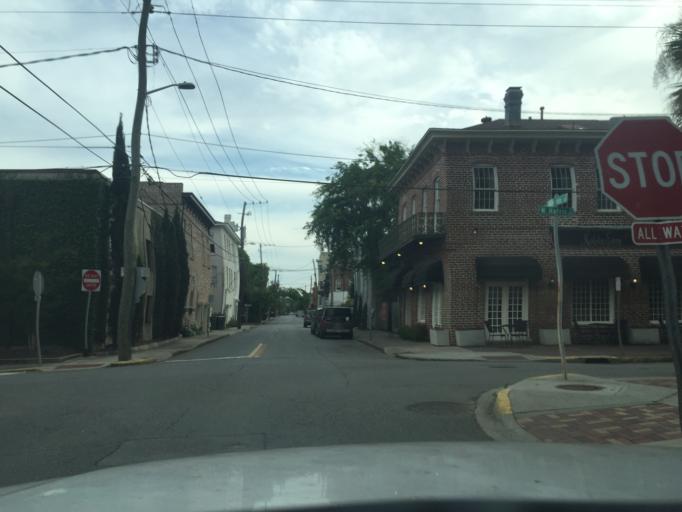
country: US
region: Georgia
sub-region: Chatham County
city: Savannah
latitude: 32.0748
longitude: -81.0972
